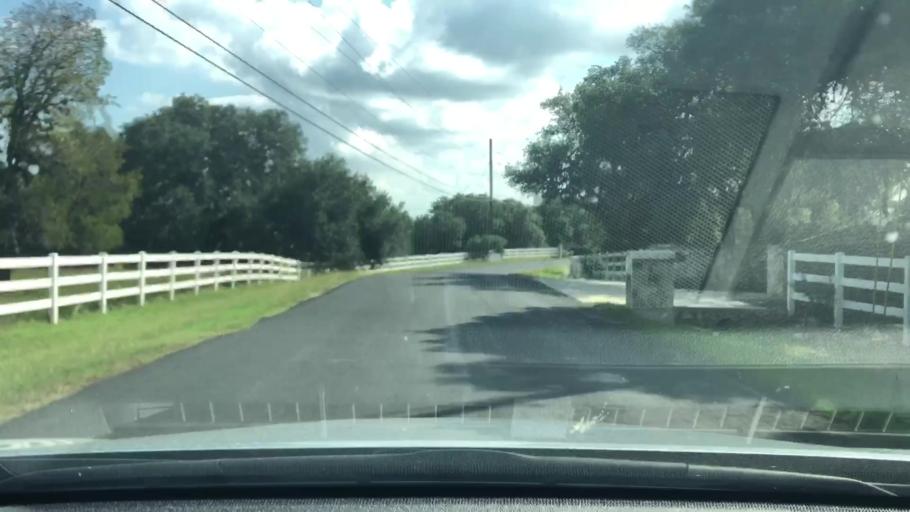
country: US
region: Texas
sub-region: Bexar County
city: Fair Oaks Ranch
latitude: 29.7694
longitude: -98.6253
